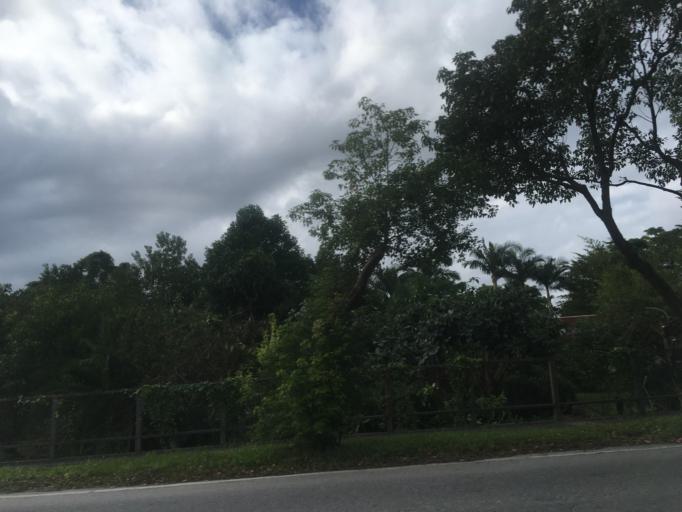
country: TW
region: Taiwan
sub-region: Yilan
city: Yilan
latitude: 24.6885
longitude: 121.7372
